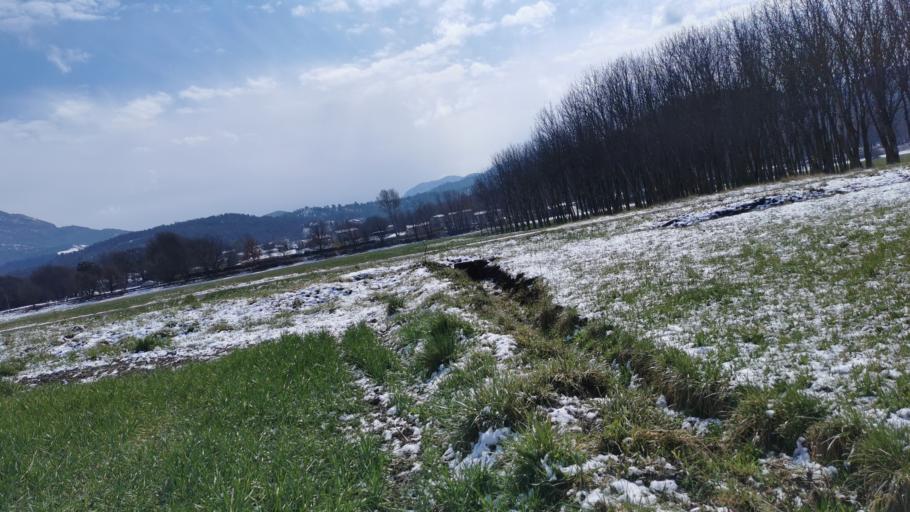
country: FR
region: Provence-Alpes-Cote d'Azur
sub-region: Departement des Alpes-de-Haute-Provence
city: Mallemoisson
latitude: 44.0554
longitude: 6.1668
